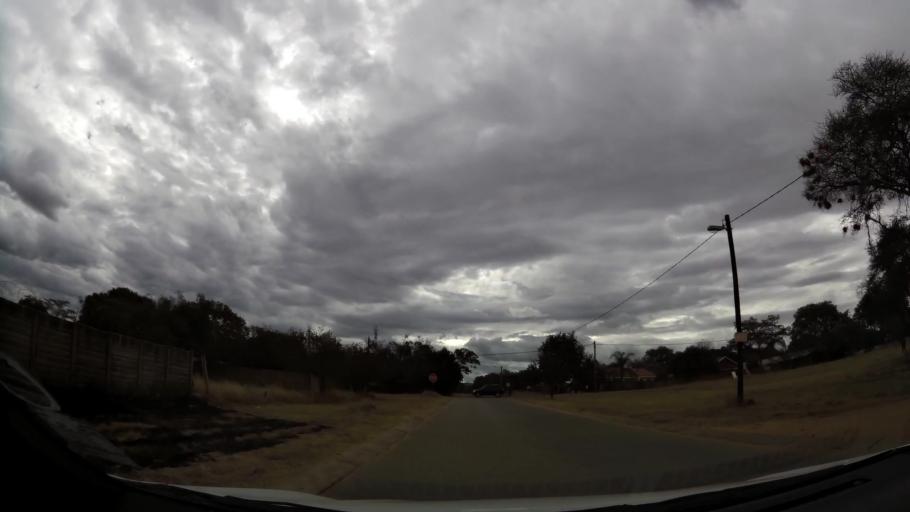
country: ZA
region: Limpopo
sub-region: Waterberg District Municipality
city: Modimolle
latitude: -24.6998
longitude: 28.4174
